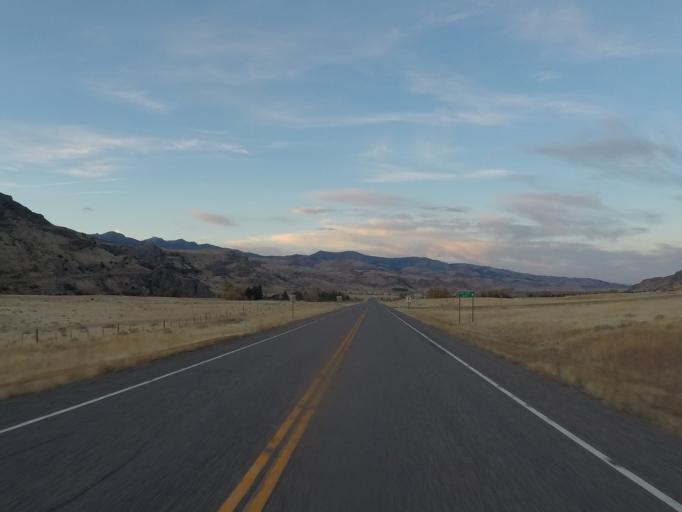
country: US
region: Montana
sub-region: Gallatin County
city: Bozeman
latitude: 45.2453
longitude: -110.8695
